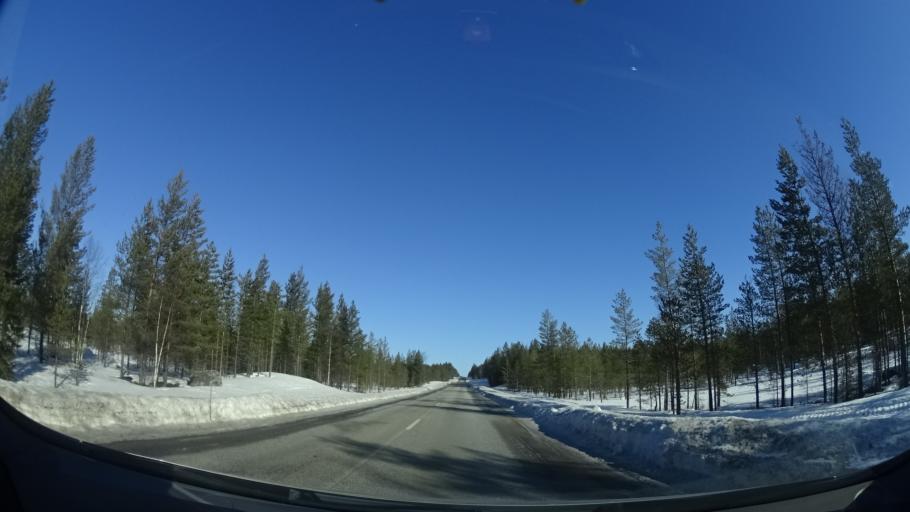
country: SE
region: Vaesterbotten
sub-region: Skelleftea Kommun
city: Langsele
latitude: 65.0840
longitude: 20.0751
